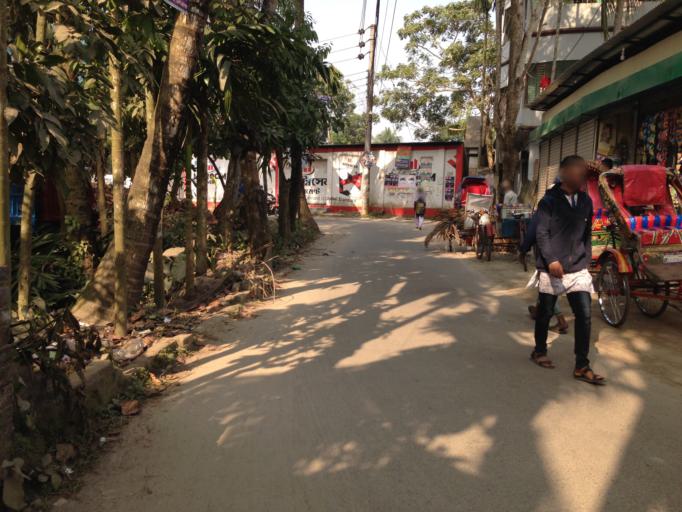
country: BD
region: Chittagong
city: Lakshmipur
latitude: 22.9367
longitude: 90.8320
